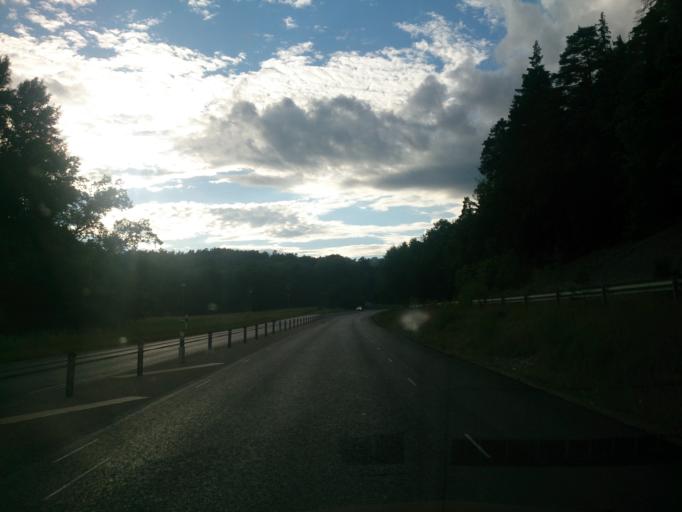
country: SE
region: OEstergoetland
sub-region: Norrkopings Kommun
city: Jursla
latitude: 58.6735
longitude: 16.1551
